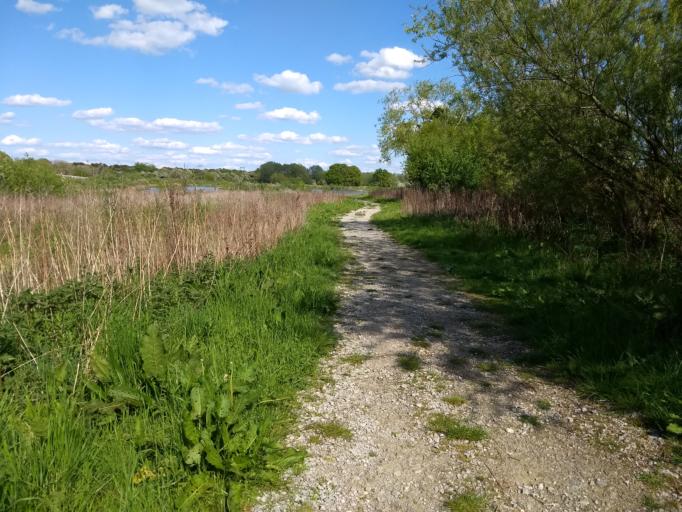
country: GB
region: England
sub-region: Milton Keynes
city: Castlethorpe
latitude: 52.0727
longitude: -0.8234
